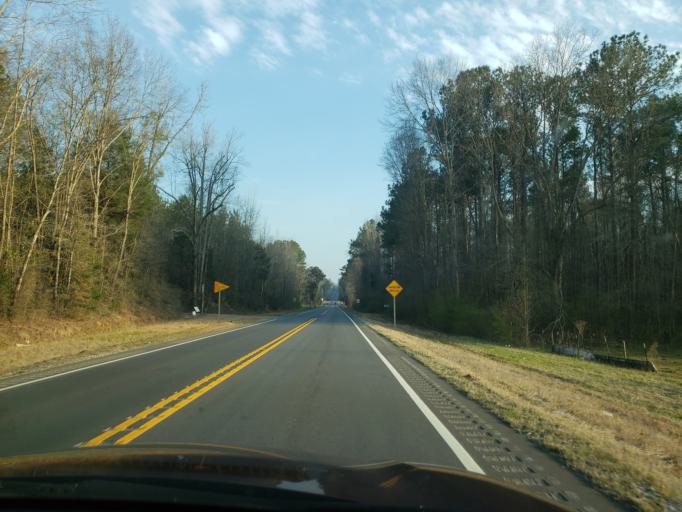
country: US
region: Alabama
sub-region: Hale County
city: Greensboro
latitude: 32.8234
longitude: -87.6017
